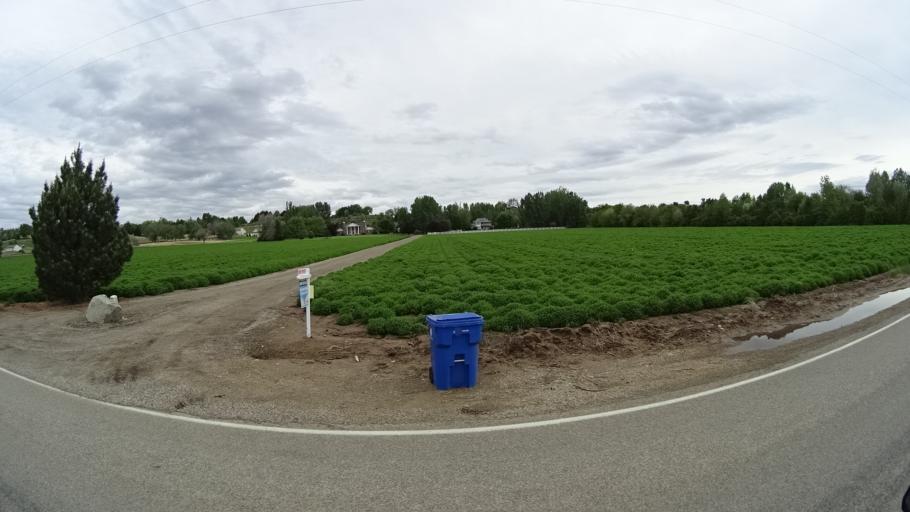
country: US
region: Idaho
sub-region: Ada County
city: Star
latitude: 43.7173
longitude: -116.5068
